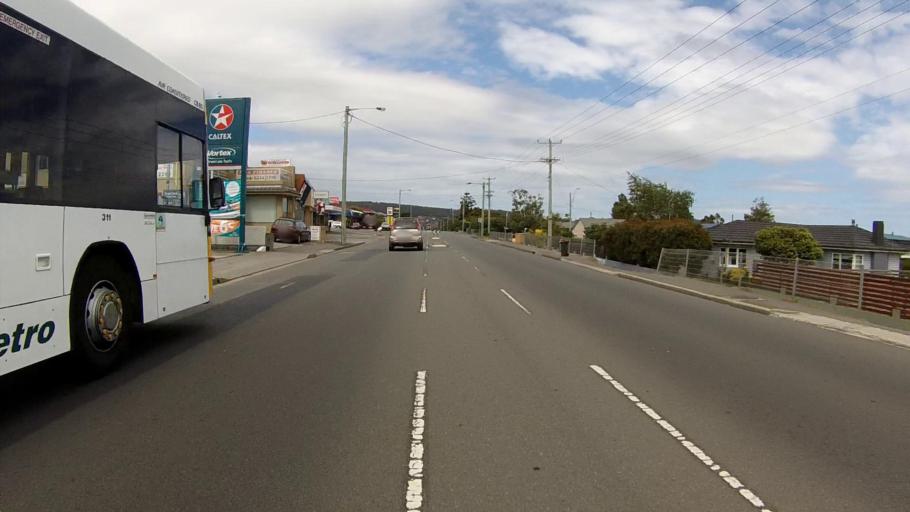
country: AU
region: Tasmania
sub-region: Clarence
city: Bellerive
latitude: -42.8758
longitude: 147.3773
